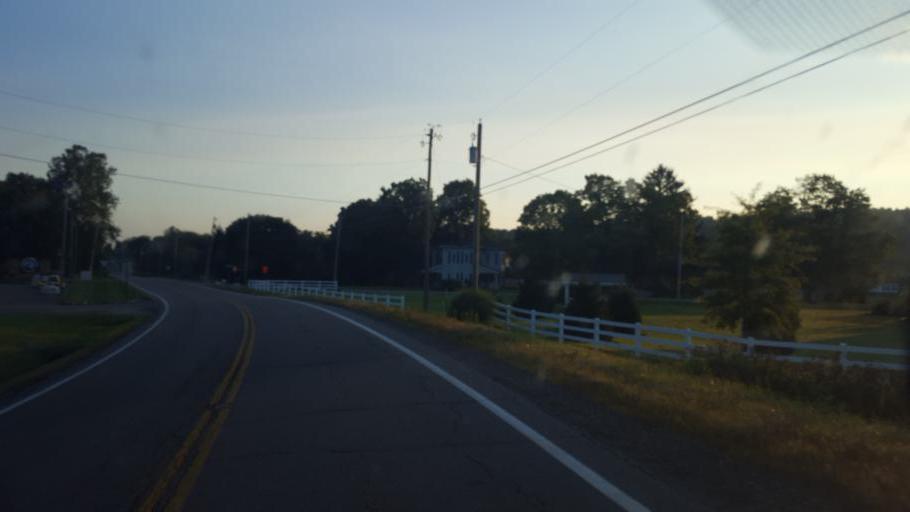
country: US
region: Ohio
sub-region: Sandusky County
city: Bellville
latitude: 40.6014
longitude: -82.5141
